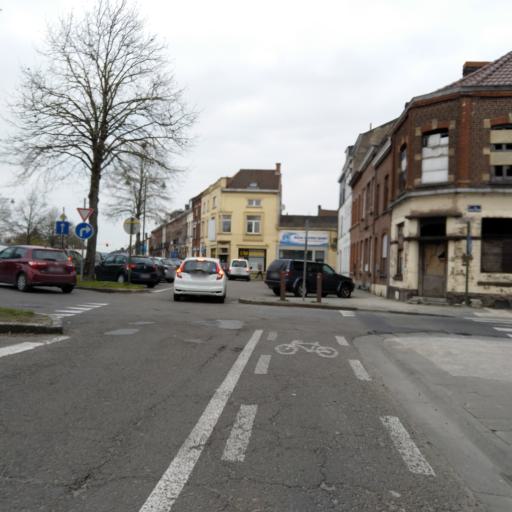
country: BE
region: Wallonia
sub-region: Province du Hainaut
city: Mons
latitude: 50.4641
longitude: 3.9581
